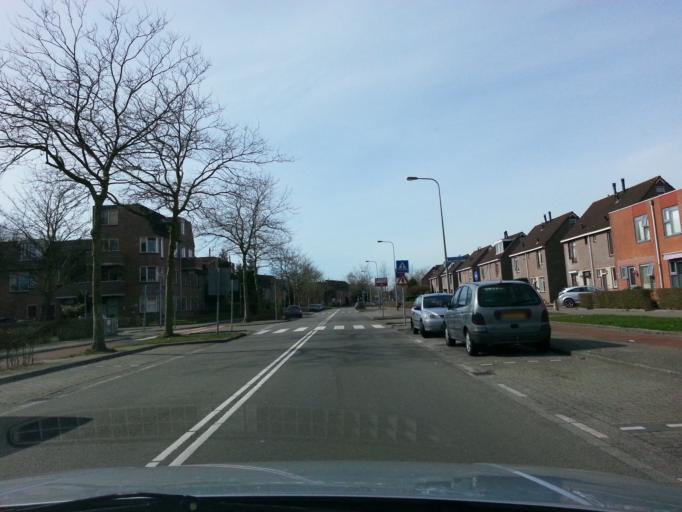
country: NL
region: Groningen
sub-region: Gemeente Groningen
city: Oosterpark
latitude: 53.2479
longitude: 6.6010
